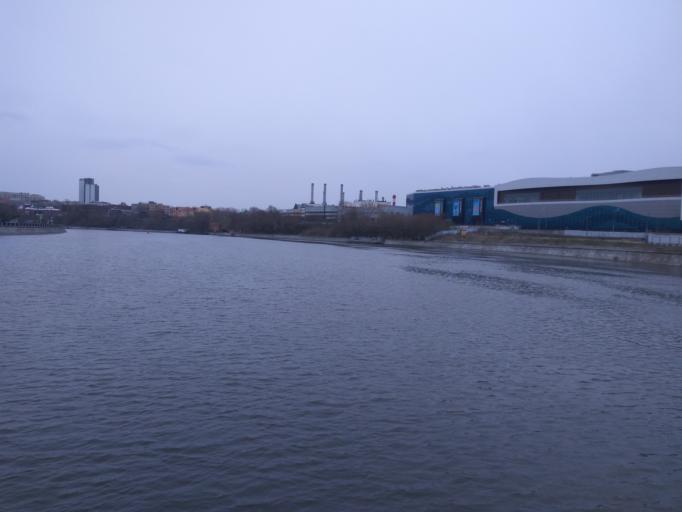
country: RU
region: Moscow
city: Zamoskvorech'ye
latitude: 55.7073
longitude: 37.6381
